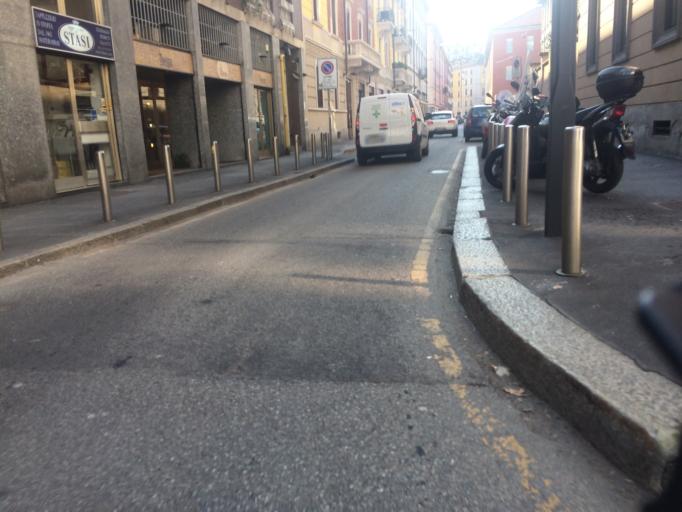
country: IT
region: Lombardy
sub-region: Citta metropolitana di Milano
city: Milano
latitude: 45.4780
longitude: 9.1741
